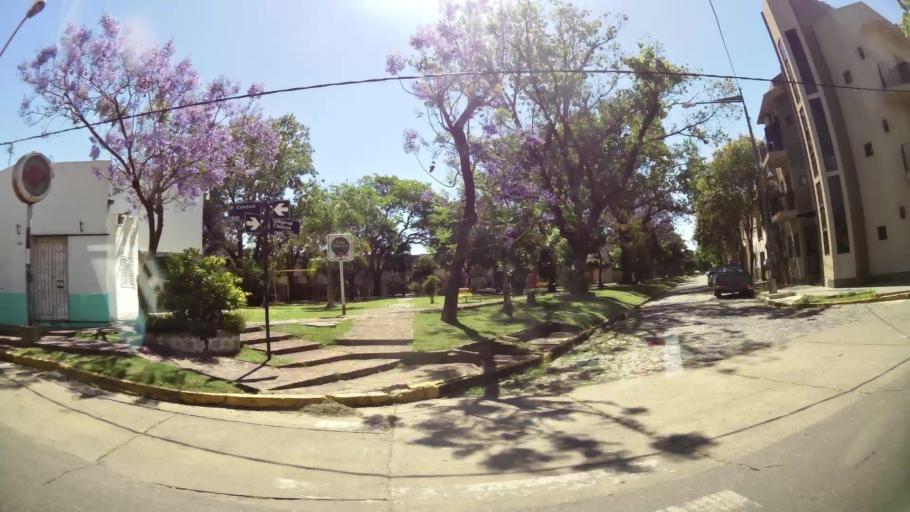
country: AR
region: Santa Fe
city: Santa Fe de la Vera Cruz
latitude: -31.6429
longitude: -60.6972
